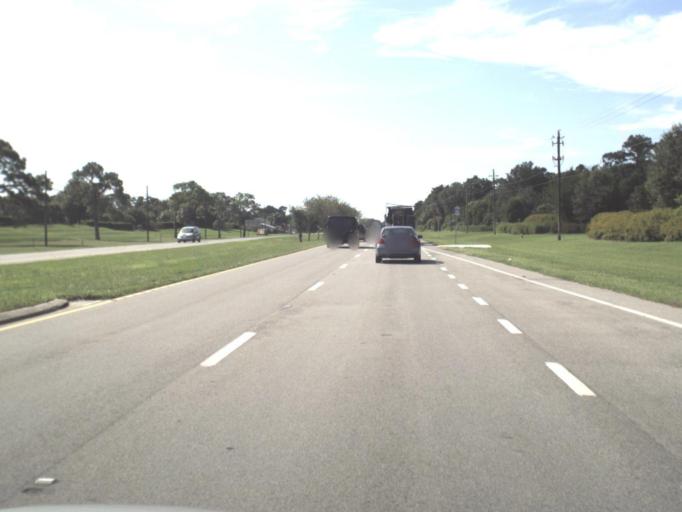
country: US
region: Florida
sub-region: Sarasota County
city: Osprey
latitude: 27.2070
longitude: -82.4904
